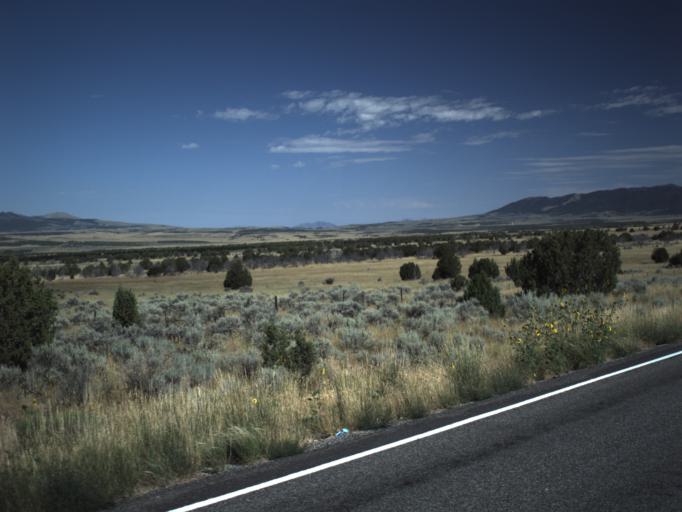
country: US
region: Utah
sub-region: Juab County
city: Mona
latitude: 39.8527
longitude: -112.1381
